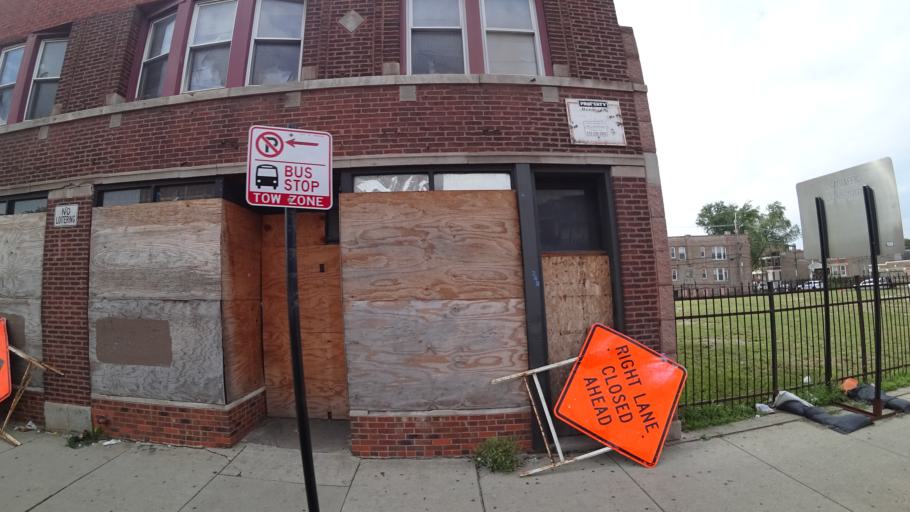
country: US
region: Illinois
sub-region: Cook County
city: Cicero
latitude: 41.8754
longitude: -87.7451
